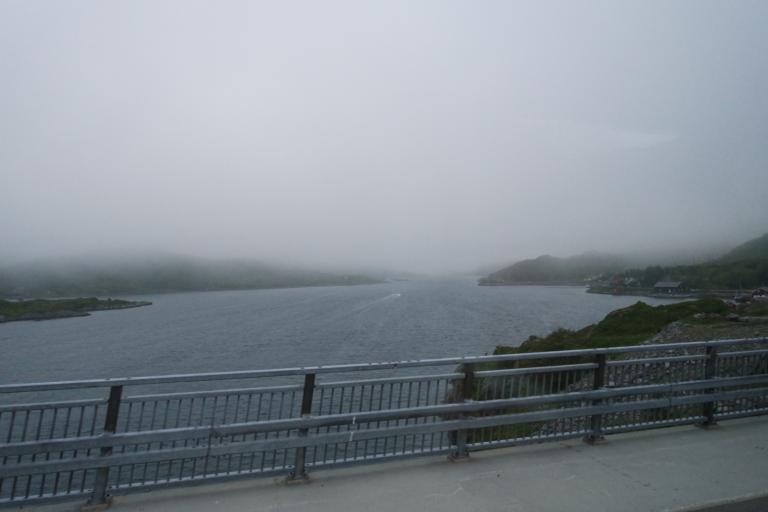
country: NO
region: Nordland
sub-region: Flakstad
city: Ramberg
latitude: 68.0167
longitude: 13.1751
